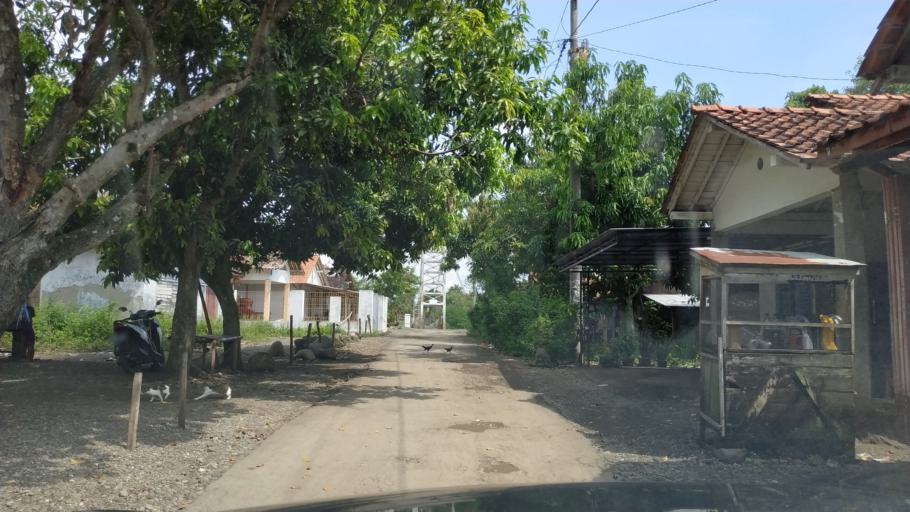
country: ID
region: Central Java
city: Margasari
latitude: -7.0951
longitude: 108.9738
